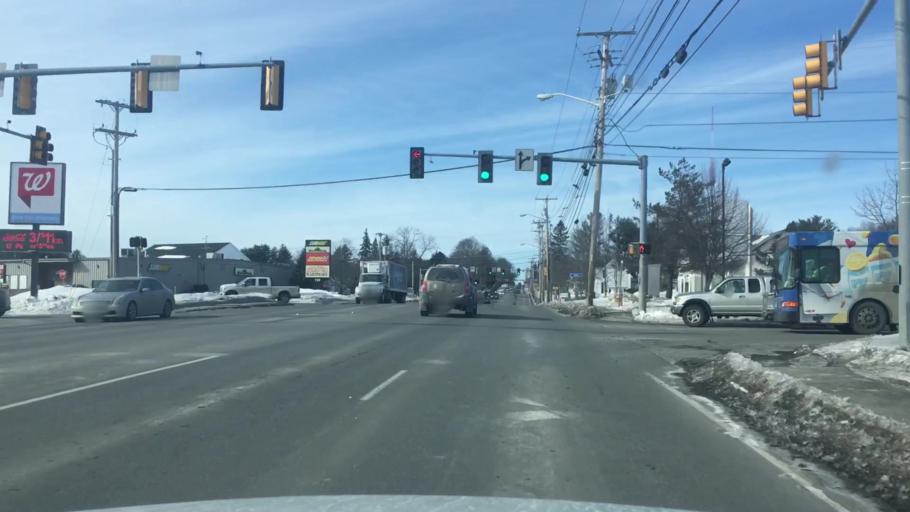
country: US
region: Maine
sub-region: Penobscot County
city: Bangor
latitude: 44.8245
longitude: -68.7803
